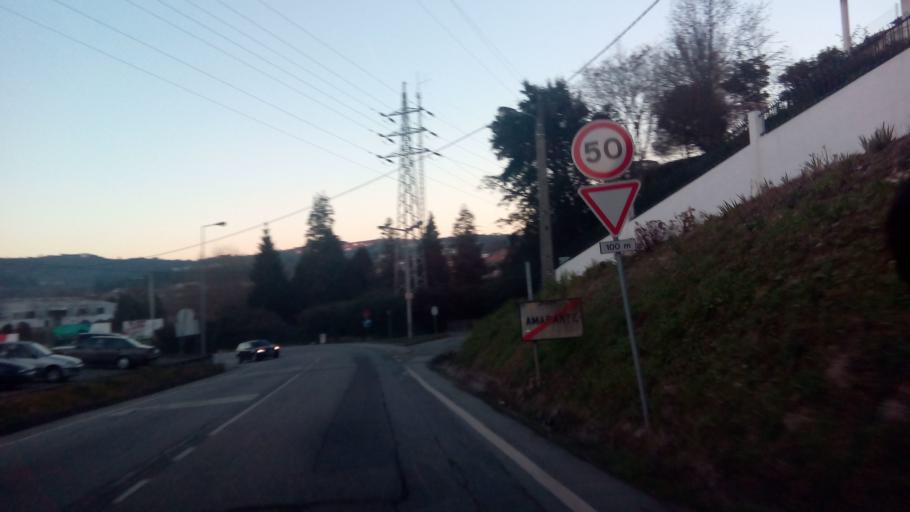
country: PT
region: Porto
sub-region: Amarante
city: Teloes
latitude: 41.2922
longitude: -8.0979
